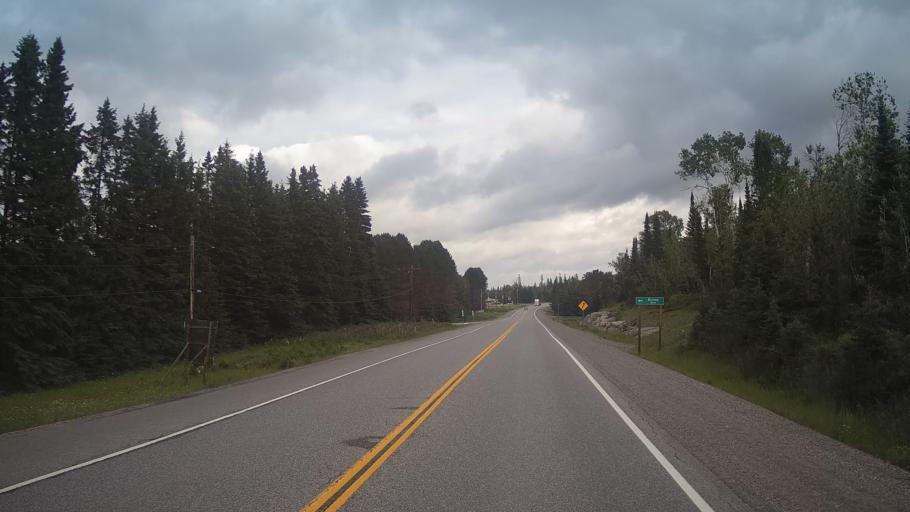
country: CA
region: Ontario
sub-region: Rainy River District
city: Atikokan
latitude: 49.0240
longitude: -90.4490
